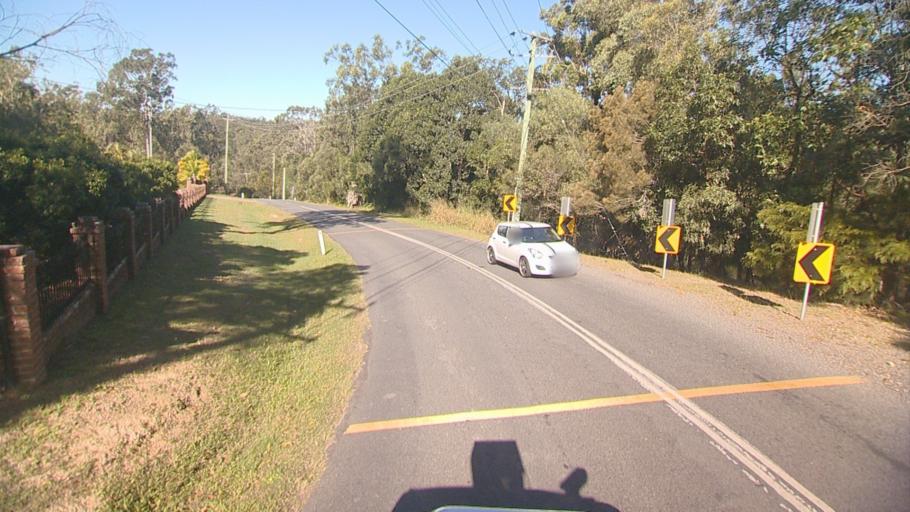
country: AU
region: Queensland
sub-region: Logan
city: Springwood
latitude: -27.6060
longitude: 153.1732
